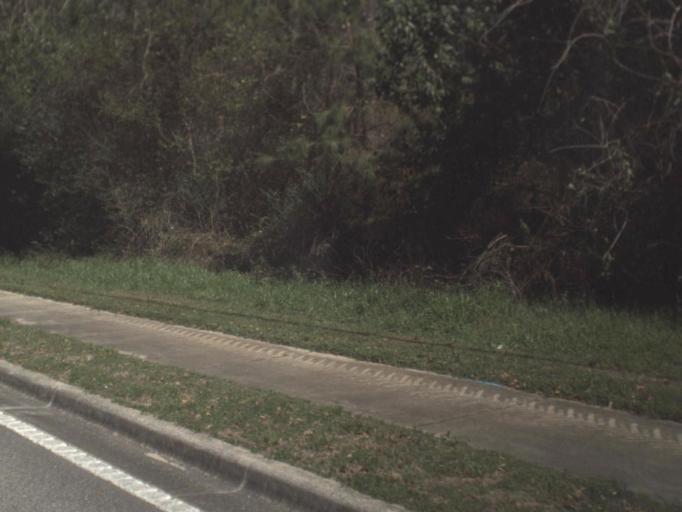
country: US
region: Florida
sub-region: Gadsden County
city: Quincy
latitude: 30.5495
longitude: -84.5920
